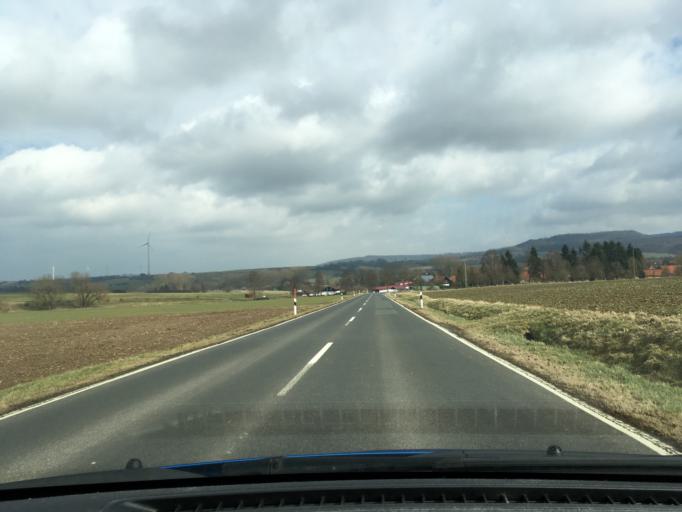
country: DE
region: Lower Saxony
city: Buhren
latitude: 51.5048
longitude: 9.7034
